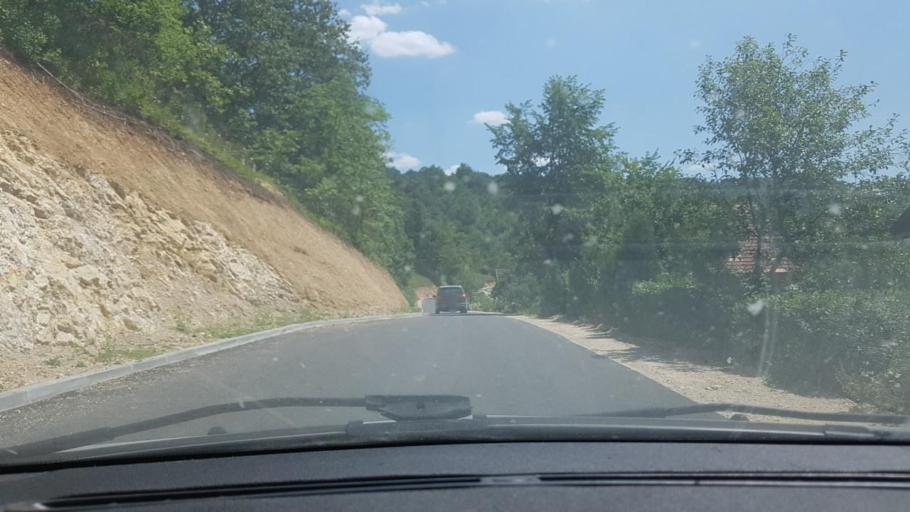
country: BA
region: Federation of Bosnia and Herzegovina
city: Orasac
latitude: 44.6409
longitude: 16.0408
